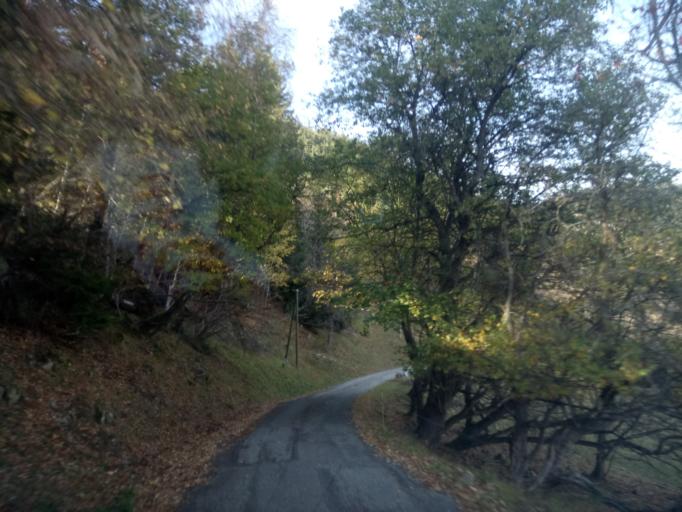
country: FR
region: Rhone-Alpes
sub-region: Departement de la Savoie
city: La Chambre
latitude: 45.3853
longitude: 6.3070
